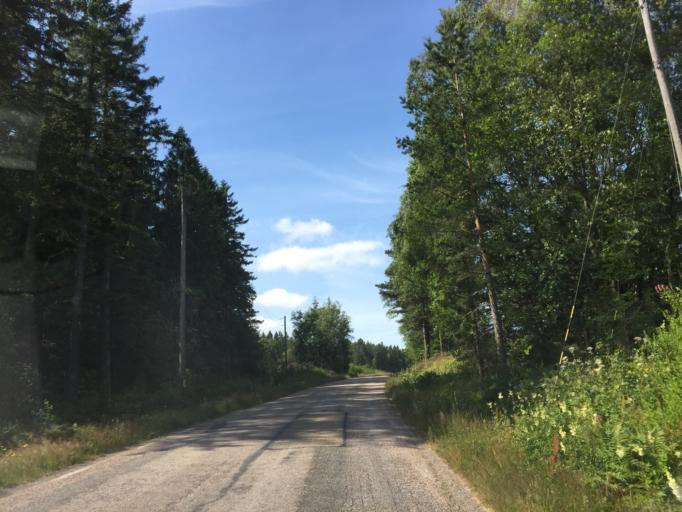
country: SE
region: Vaestra Goetaland
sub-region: Orust
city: Henan
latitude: 58.2957
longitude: 11.6580
